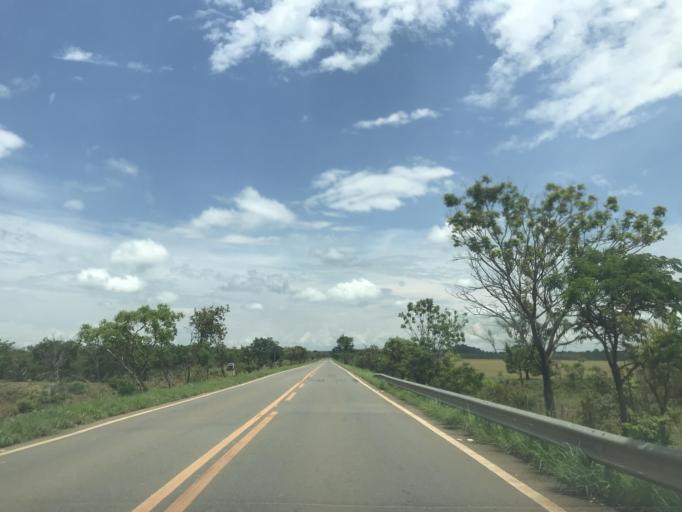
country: BR
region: Goias
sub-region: Luziania
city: Luziania
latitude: -16.3990
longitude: -48.1315
